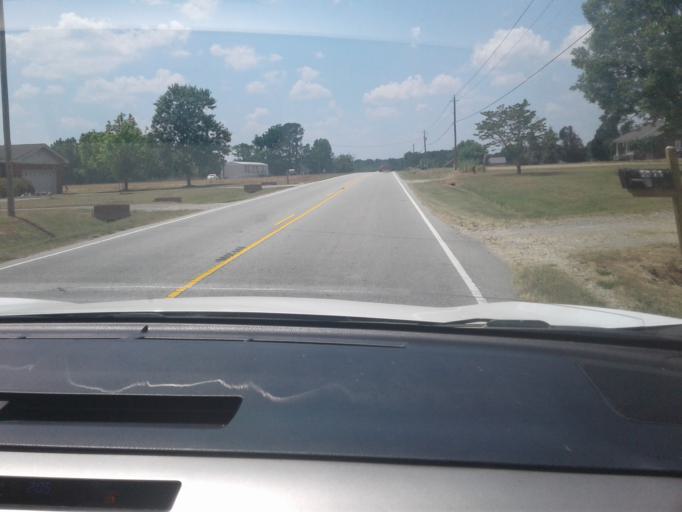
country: US
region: North Carolina
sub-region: Johnston County
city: Benson
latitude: 35.3926
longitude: -78.5891
